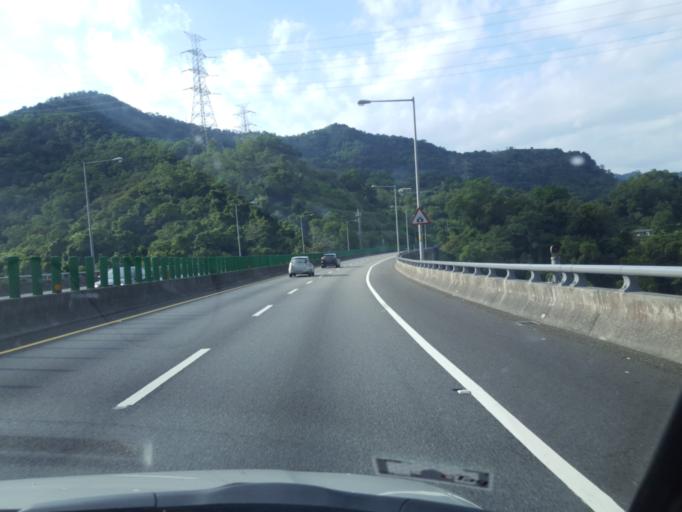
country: TW
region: Taipei
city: Taipei
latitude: 24.9913
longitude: 121.6550
